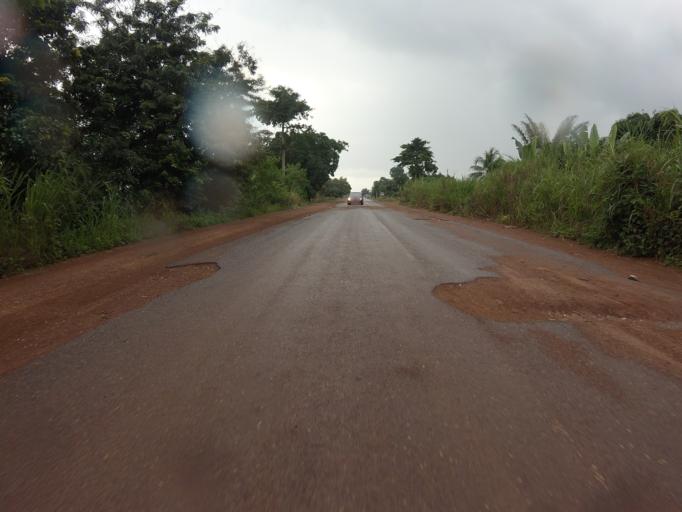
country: GH
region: Volta
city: Hohoe
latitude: 7.0383
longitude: 0.4269
